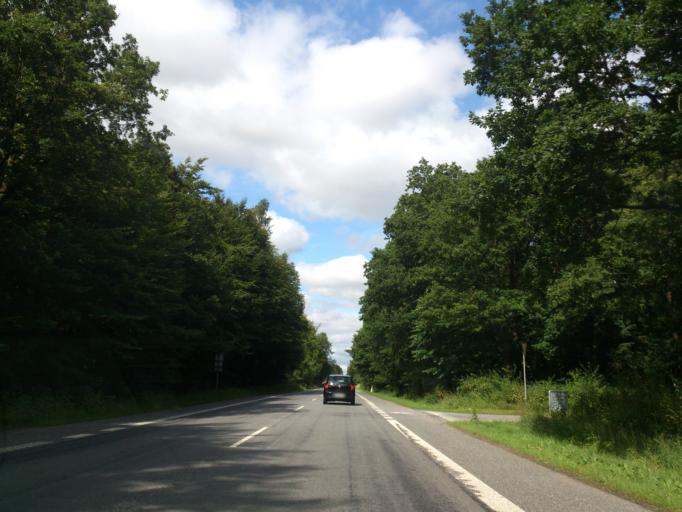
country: DK
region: South Denmark
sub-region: Aabenraa Kommune
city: Krusa
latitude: 54.8831
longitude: 9.4183
